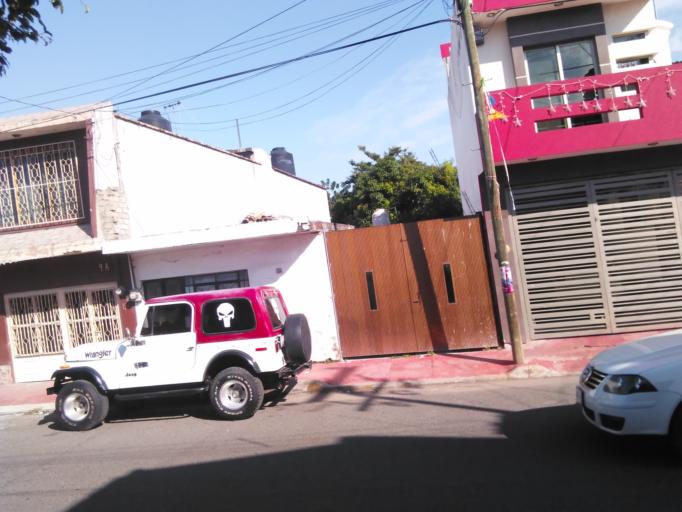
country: MX
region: Nayarit
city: Tepic
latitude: 21.4842
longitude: -104.8919
